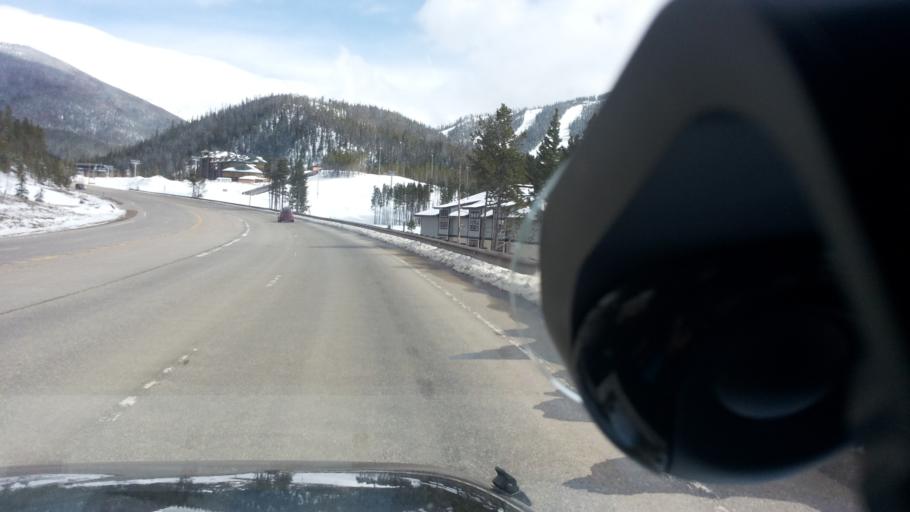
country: US
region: Colorado
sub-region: Grand County
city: Fraser
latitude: 39.8867
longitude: -105.7606
